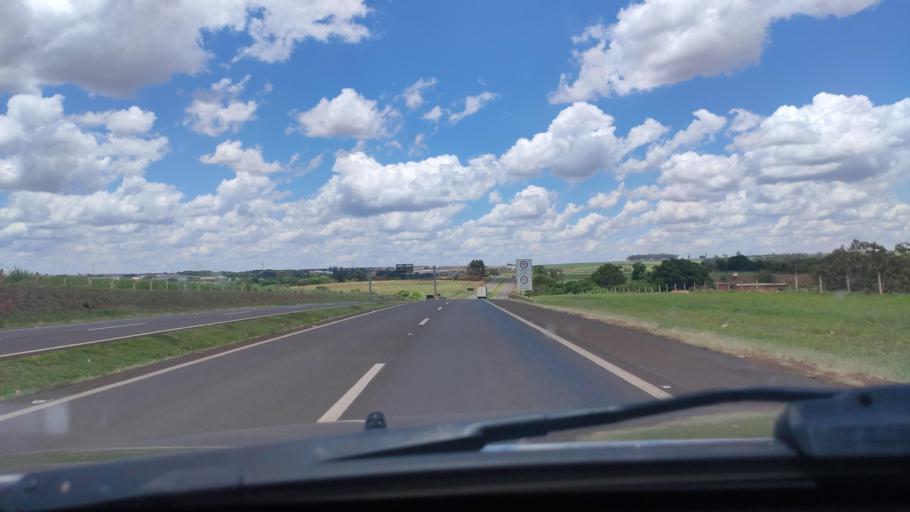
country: BR
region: Sao Paulo
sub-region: Pederneiras
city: Pederneiras
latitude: -22.3280
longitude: -48.7424
